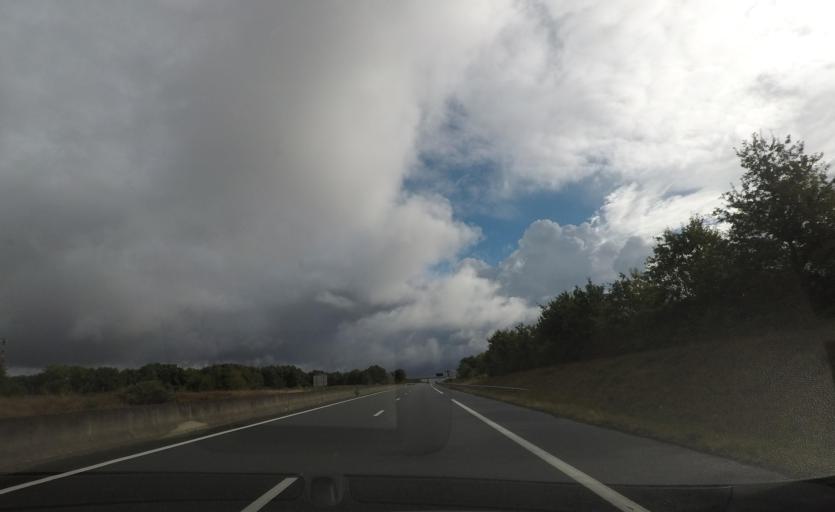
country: FR
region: Pays de la Loire
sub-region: Departement de la Vendee
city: La Roche-sur-Yon
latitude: 46.6562
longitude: -1.3806
